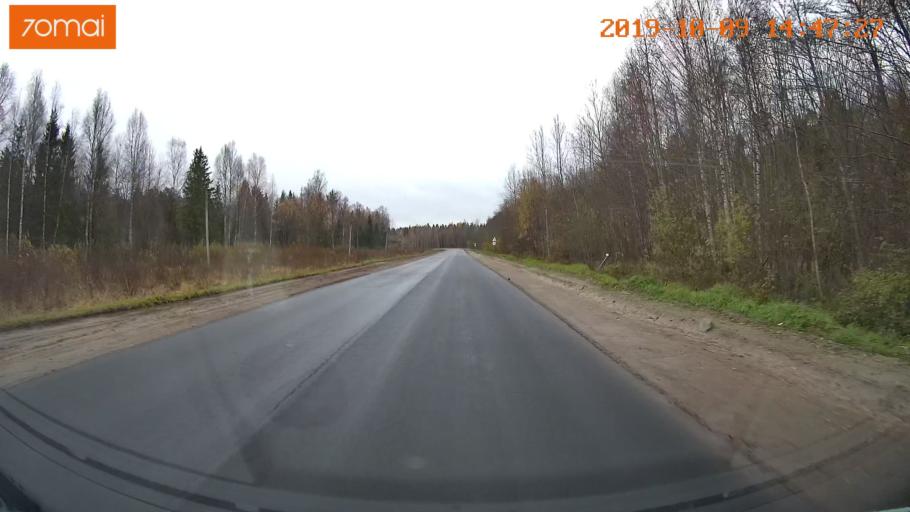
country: RU
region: Kostroma
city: Buy
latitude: 58.4178
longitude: 41.5725
